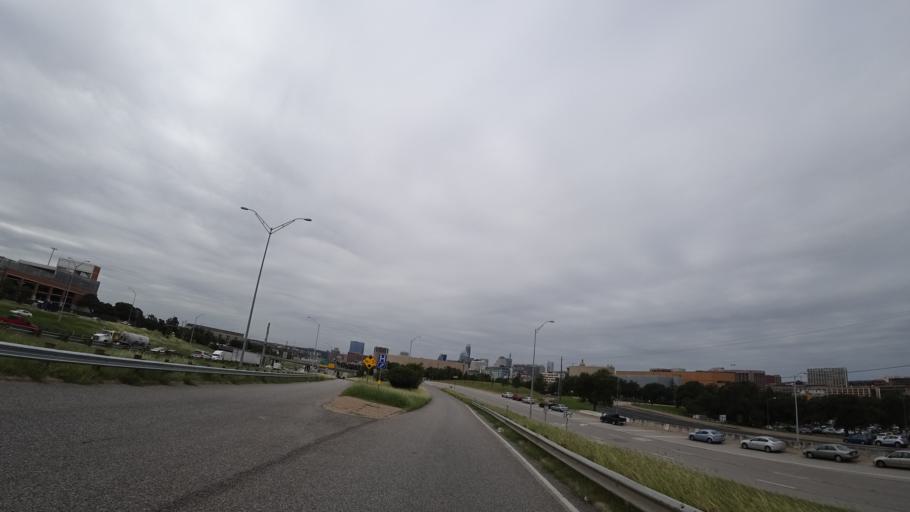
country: US
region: Texas
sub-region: Travis County
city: Austin
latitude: 30.2811
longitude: -97.7290
